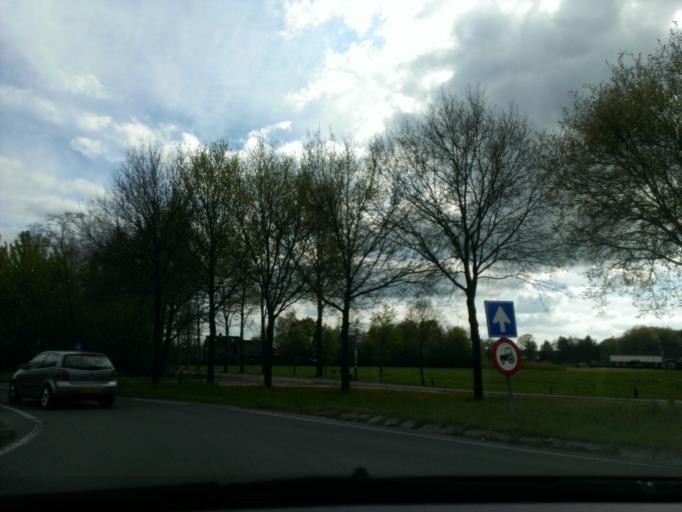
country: NL
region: Overijssel
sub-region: Gemeente Hof van Twente
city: Goor
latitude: 52.2946
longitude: 6.5534
